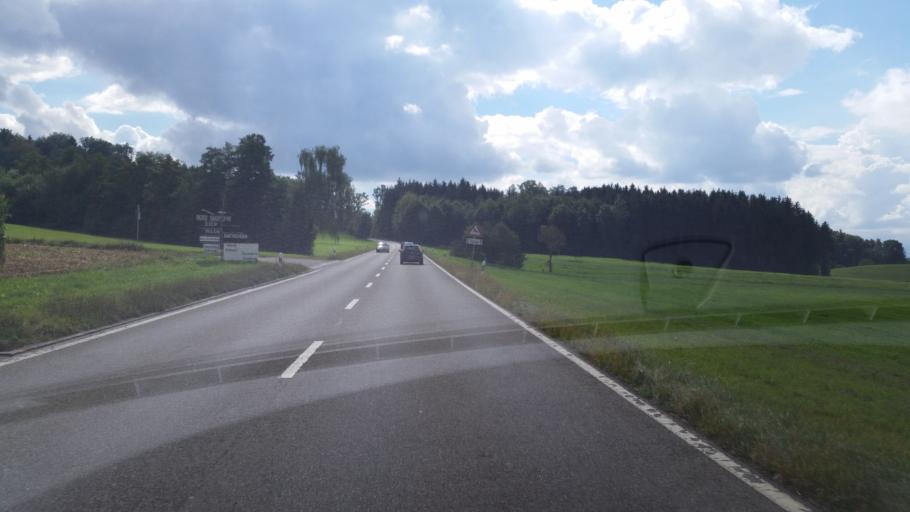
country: CH
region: Zurich
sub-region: Bezirk Affoltern
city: Affoltern / Hasenbueel
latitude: 47.2648
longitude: 8.4481
